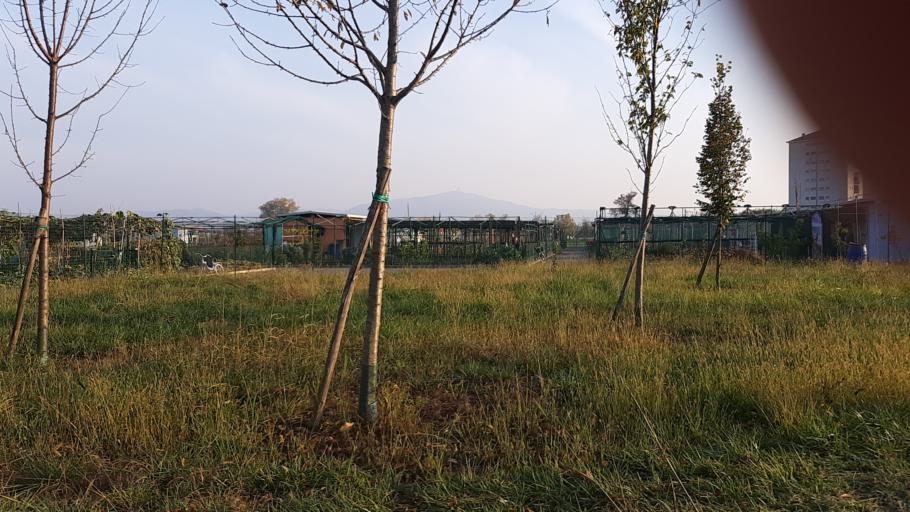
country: IT
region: Piedmont
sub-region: Provincia di Torino
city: Settimo Torinese
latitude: 45.1333
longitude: 7.7159
